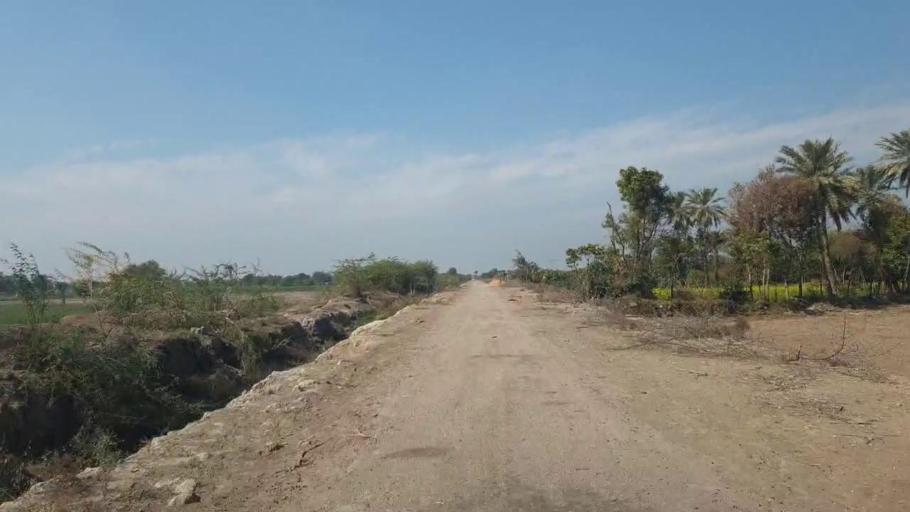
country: PK
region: Sindh
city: Shahdadpur
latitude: 25.9974
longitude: 68.5230
